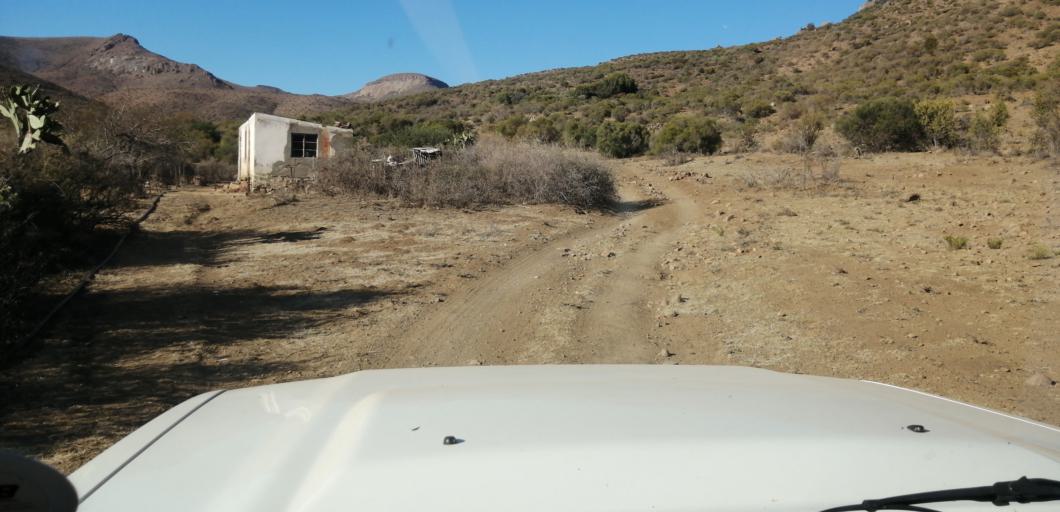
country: ZA
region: Eastern Cape
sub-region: Chris Hani District Municipality
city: Cradock
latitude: -32.1956
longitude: 25.2039
